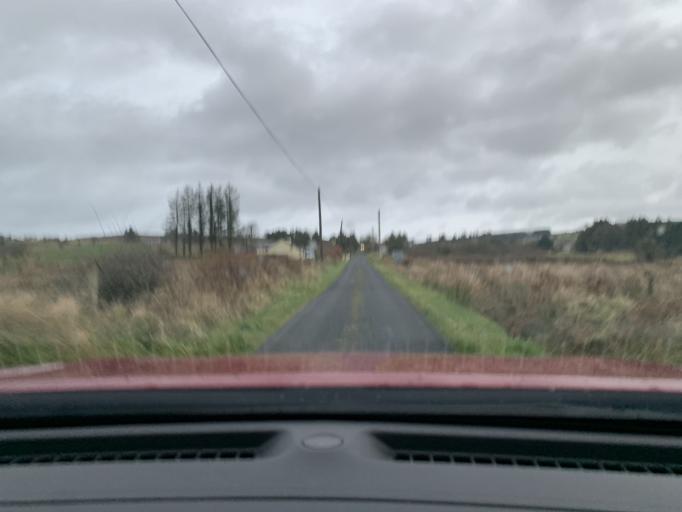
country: IE
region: Connaught
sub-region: Roscommon
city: Boyle
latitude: 53.9906
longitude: -8.3096
